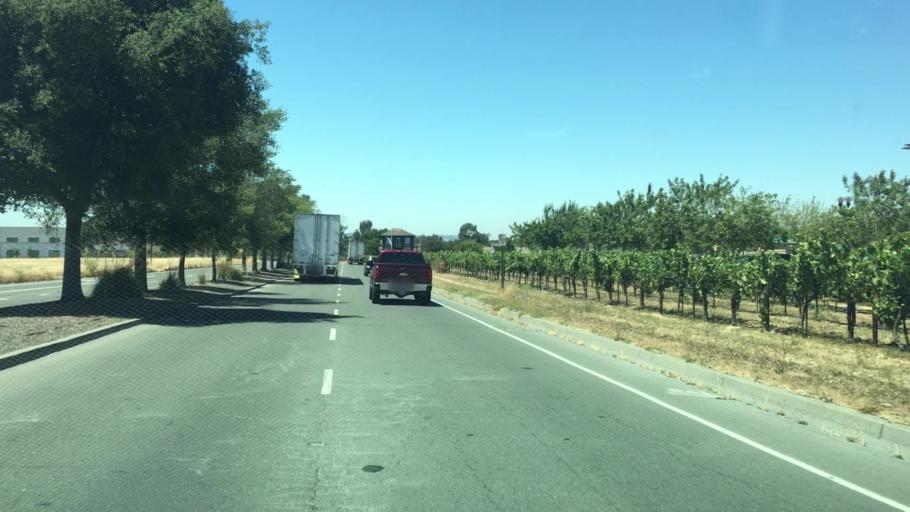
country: US
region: California
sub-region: Napa County
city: American Canyon
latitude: 38.2232
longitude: -122.2593
